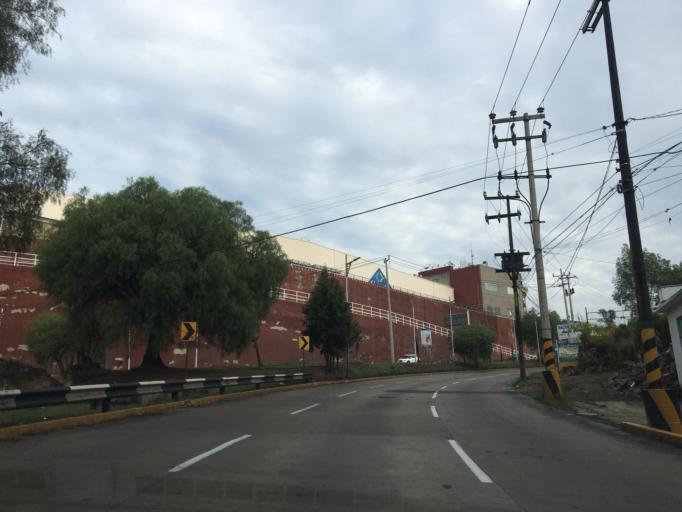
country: MX
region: Mexico
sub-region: Naucalpan de Juarez
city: Rincon Verde
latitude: 19.5126
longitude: -99.2650
